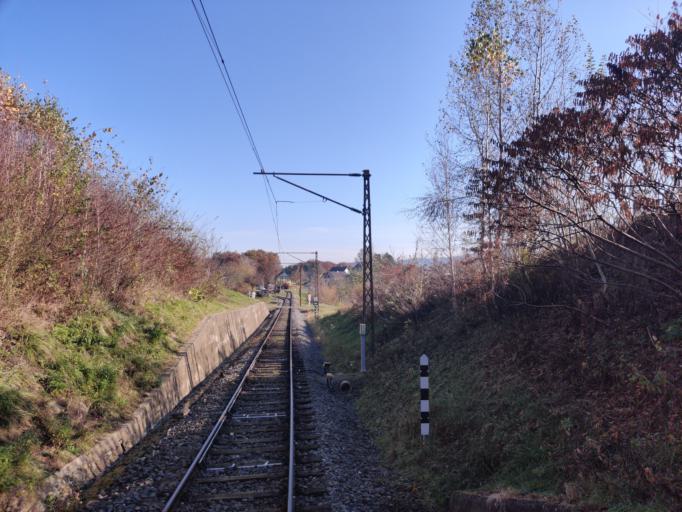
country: AT
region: Styria
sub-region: Politischer Bezirk Suedoststeiermark
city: Trautmannsdorf in Oststeiermark
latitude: 46.8789
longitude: 15.8855
